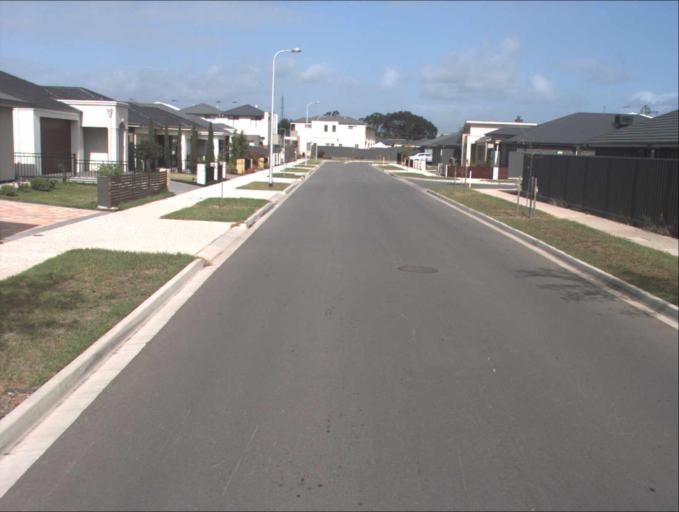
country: AU
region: South Australia
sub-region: Port Adelaide Enfield
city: Birkenhead
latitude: -34.8117
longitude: 138.5053
